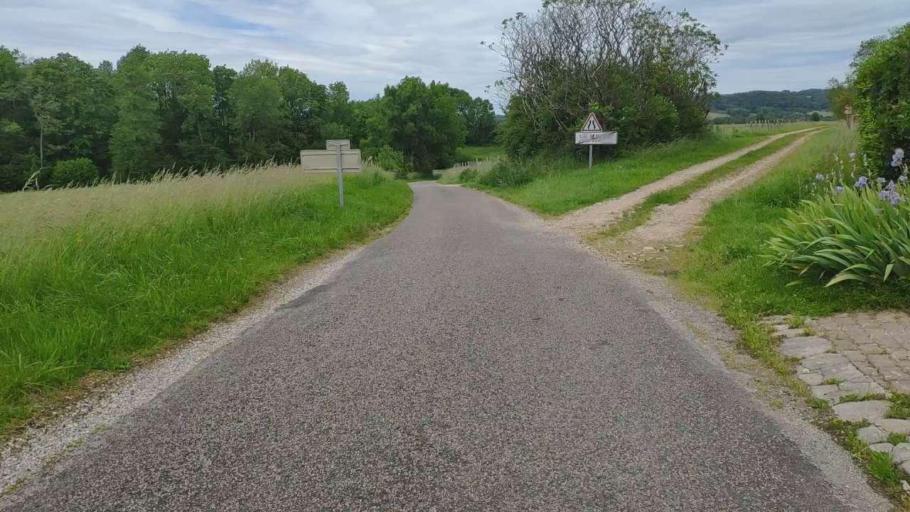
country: FR
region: Franche-Comte
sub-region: Departement du Jura
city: Perrigny
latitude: 46.7567
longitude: 5.5728
